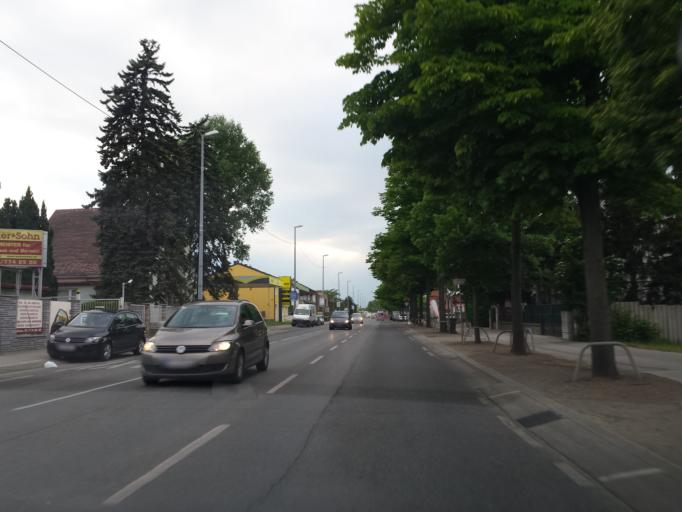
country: AT
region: Lower Austria
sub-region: Politischer Bezirk Ganserndorf
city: Gross-Enzersdorf
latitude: 48.2146
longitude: 16.5157
